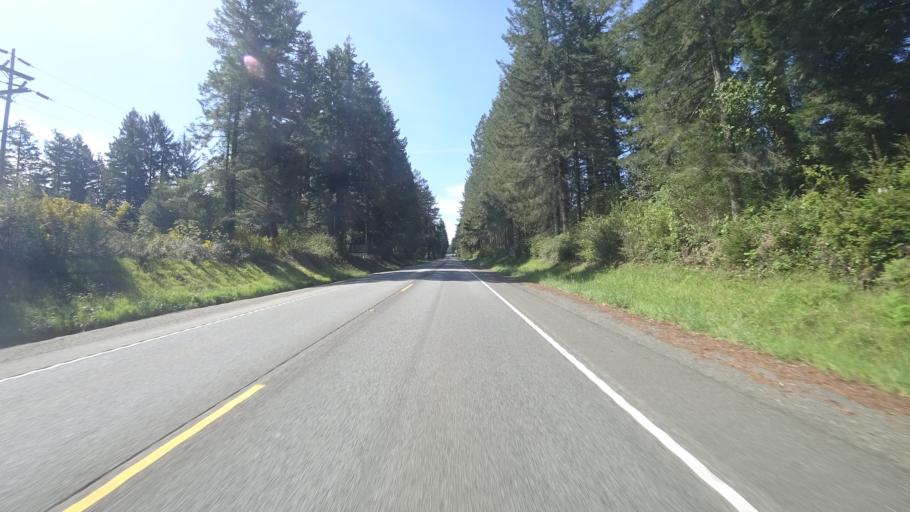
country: US
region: California
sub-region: Del Norte County
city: Bertsch-Oceanview
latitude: 41.8679
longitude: -124.1398
